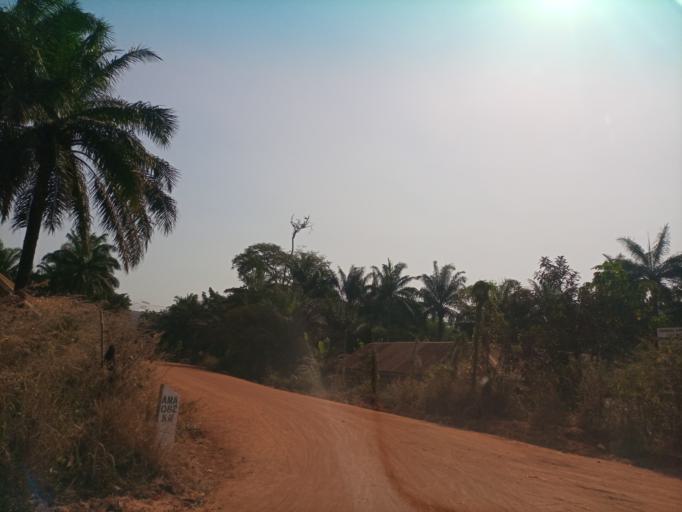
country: NG
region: Enugu
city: Aku
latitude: 6.7062
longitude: 7.3214
